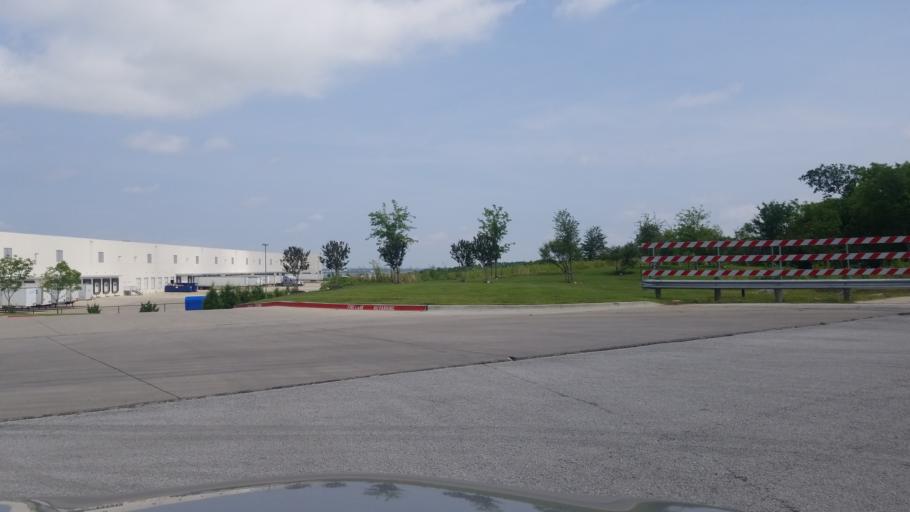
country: US
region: Texas
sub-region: Dallas County
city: Duncanville
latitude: 32.6903
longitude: -96.9519
